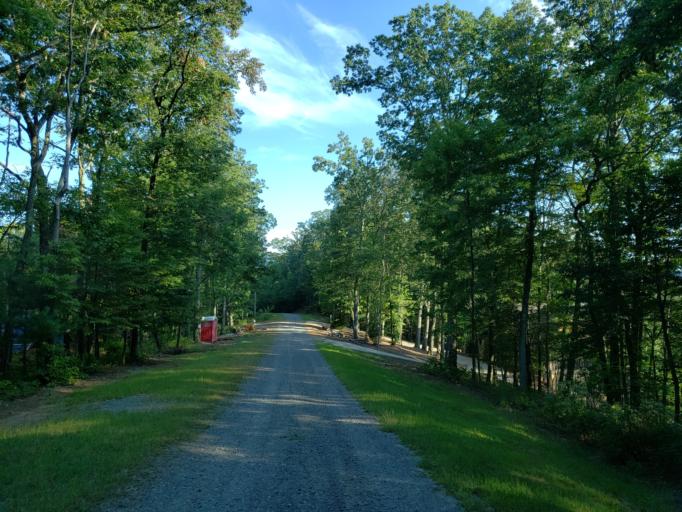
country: US
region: Georgia
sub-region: Fannin County
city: Blue Ridge
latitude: 34.6905
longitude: -84.2779
